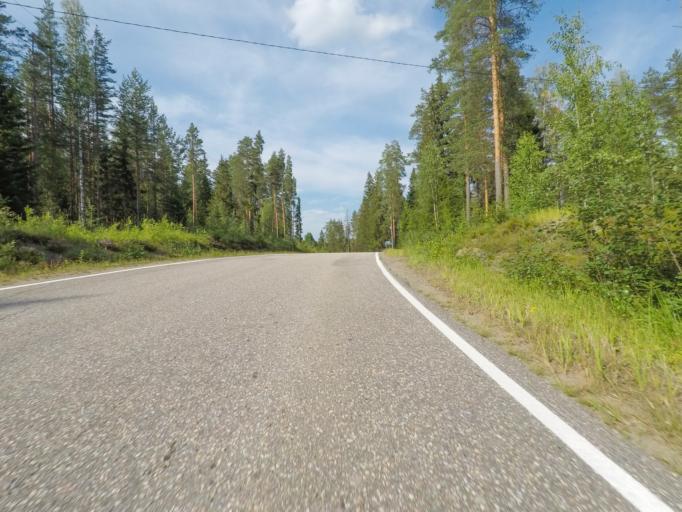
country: FI
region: Southern Savonia
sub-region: Savonlinna
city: Sulkava
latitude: 61.7799
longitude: 28.2390
